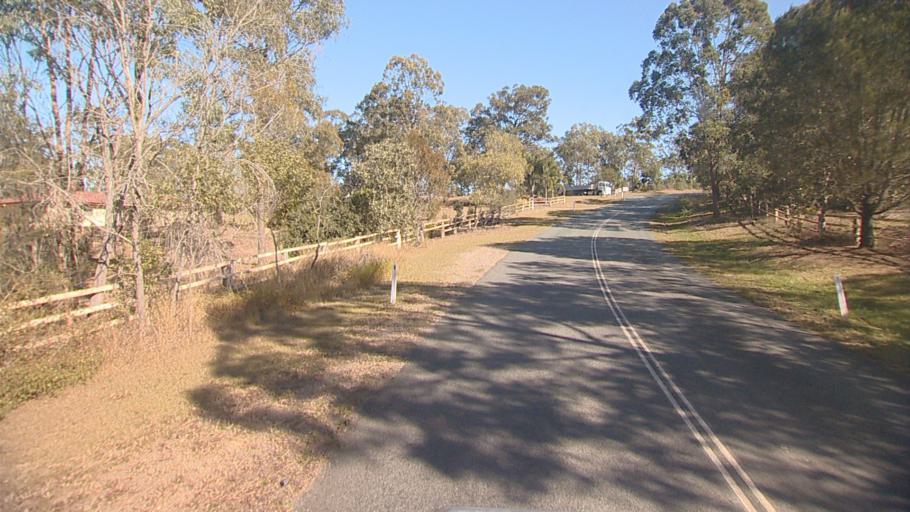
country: AU
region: Queensland
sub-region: Ipswich
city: Springfield Lakes
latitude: -27.7105
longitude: 152.9227
